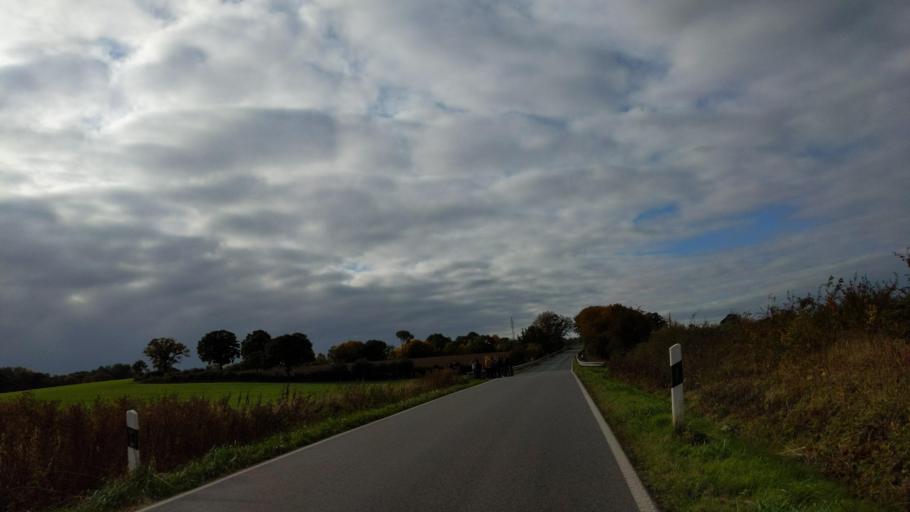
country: DE
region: Schleswig-Holstein
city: Neustadt in Holstein
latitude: 54.1007
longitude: 10.7863
